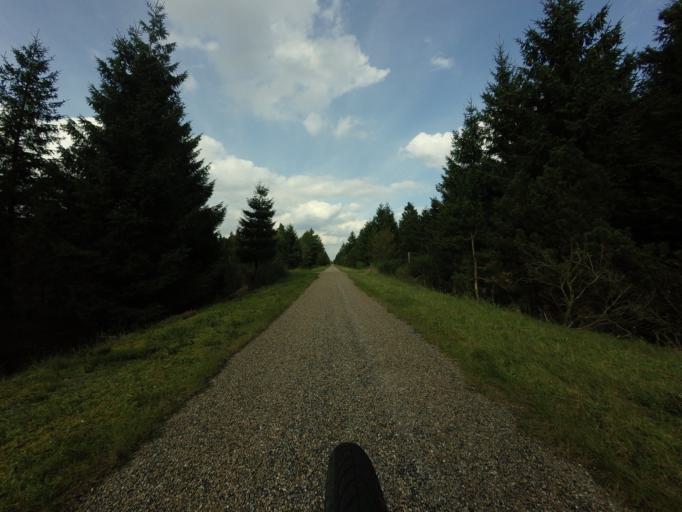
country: DK
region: Central Jutland
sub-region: Viborg Kommune
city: Karup
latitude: 56.2581
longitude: 9.1077
